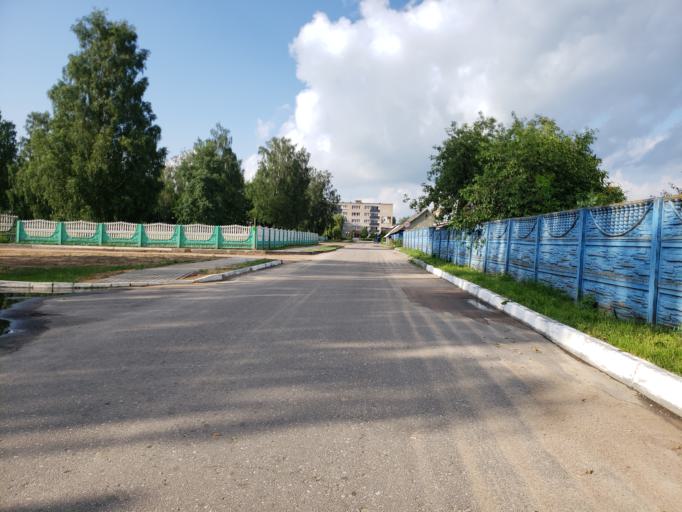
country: BY
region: Minsk
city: Chervyen'
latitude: 53.7165
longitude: 28.4025
